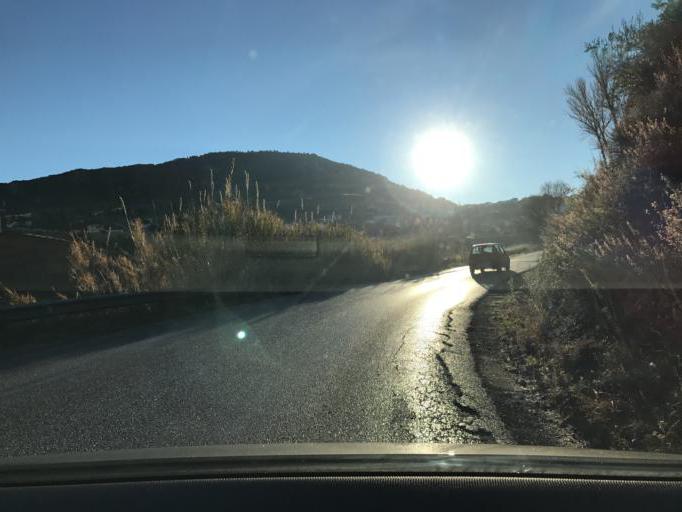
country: ES
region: Andalusia
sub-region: Provincia de Granada
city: Nivar
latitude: 37.2662
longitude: -3.5813
